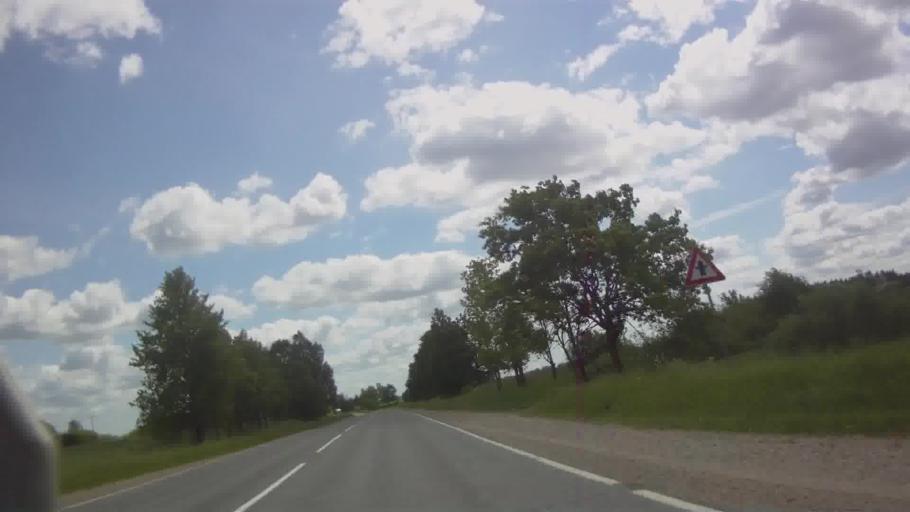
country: LV
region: Vilanu
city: Vilani
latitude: 56.5808
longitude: 26.8948
